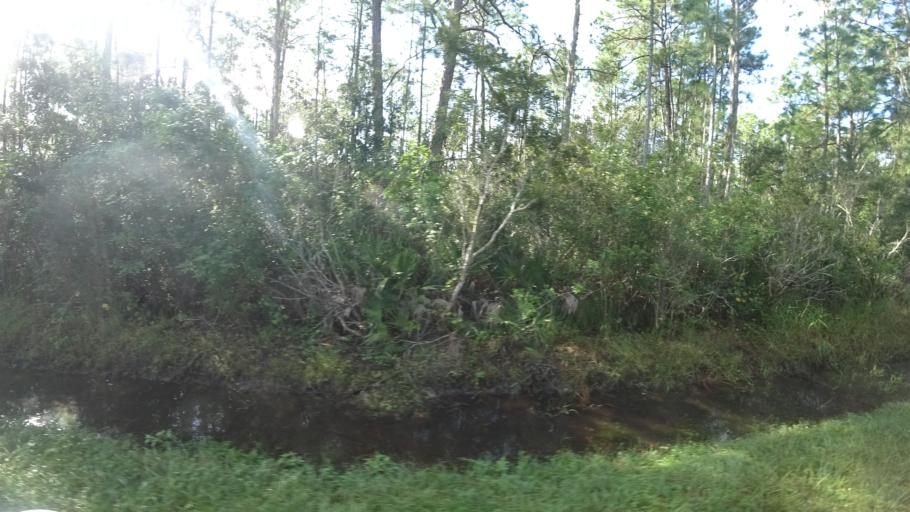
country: US
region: Florida
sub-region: Sarasota County
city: The Meadows
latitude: 27.4239
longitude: -82.3210
